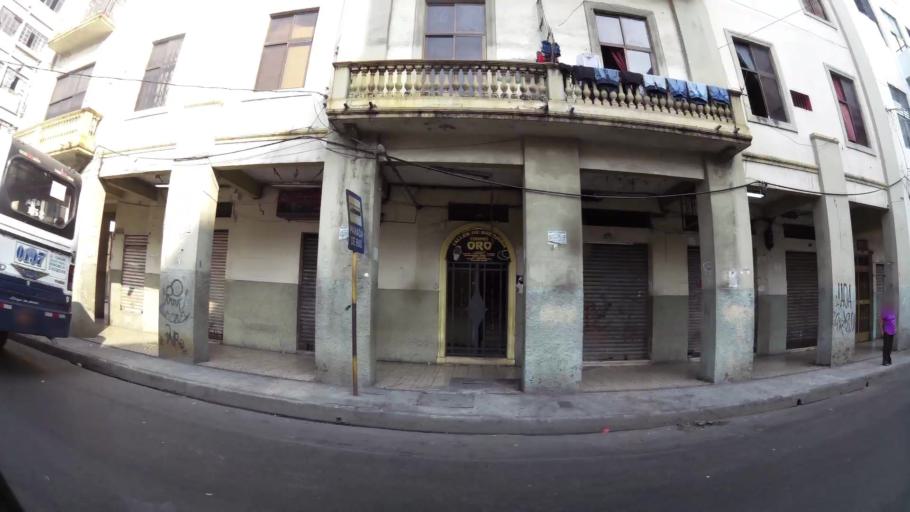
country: EC
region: Guayas
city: Guayaquil
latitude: -2.1945
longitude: -79.8859
